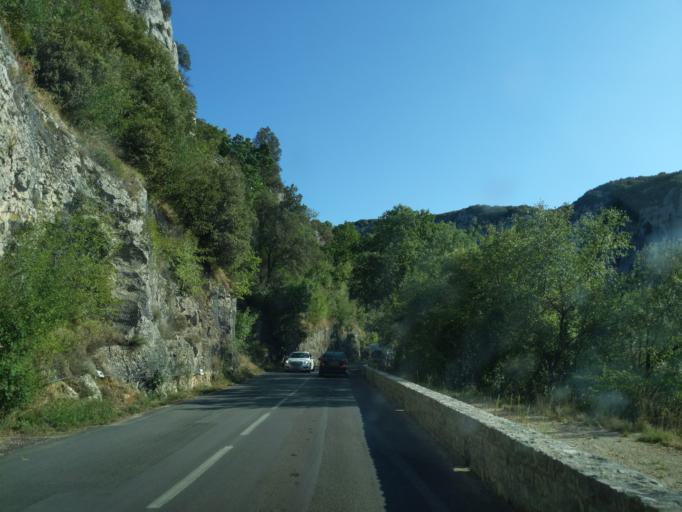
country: FR
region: Rhone-Alpes
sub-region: Departement de l'Ardeche
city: Ruoms
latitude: 44.3848
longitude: 4.4086
